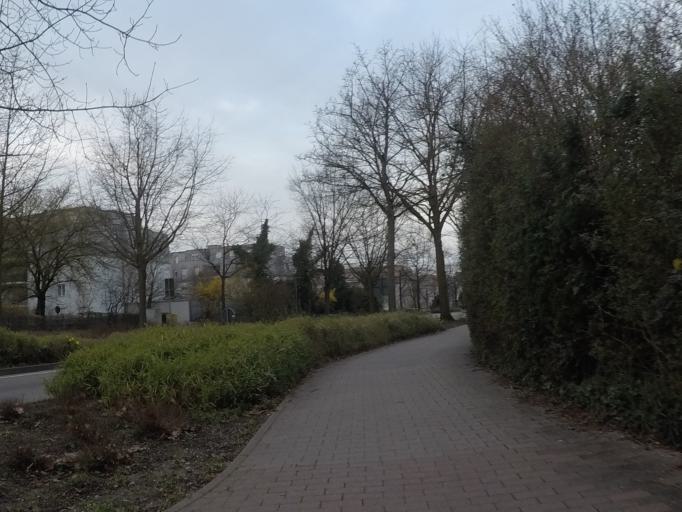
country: DE
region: Rheinland-Pfalz
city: Worth am Rhein
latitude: 49.0514
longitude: 8.2495
